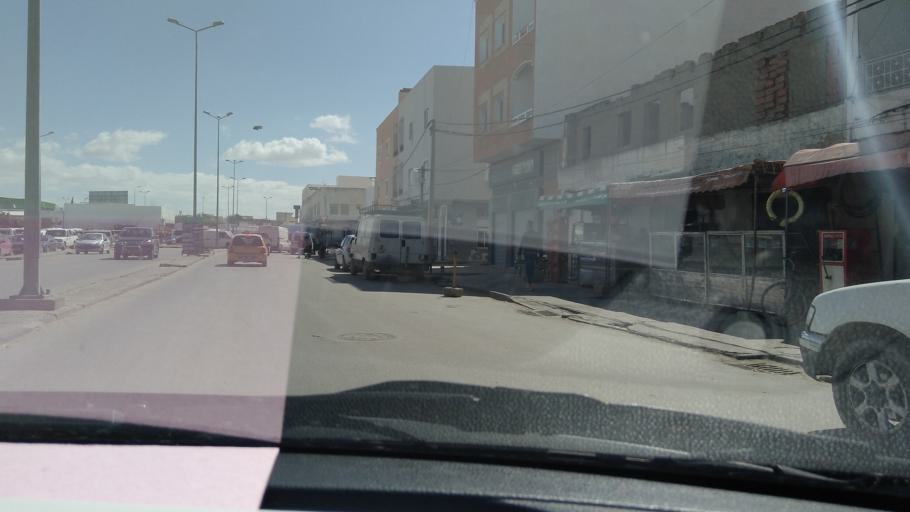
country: TN
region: Al Qayrawan
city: Kairouan
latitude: 35.6802
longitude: 10.0855
